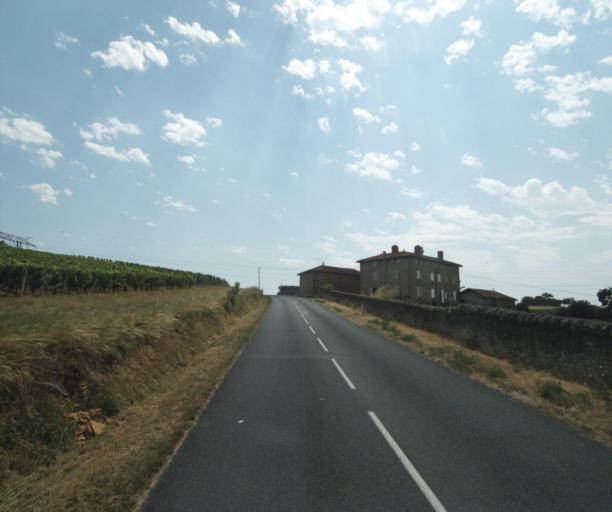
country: FR
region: Rhone-Alpes
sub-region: Departement du Rhone
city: Chatillon
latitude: 45.8706
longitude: 4.6038
